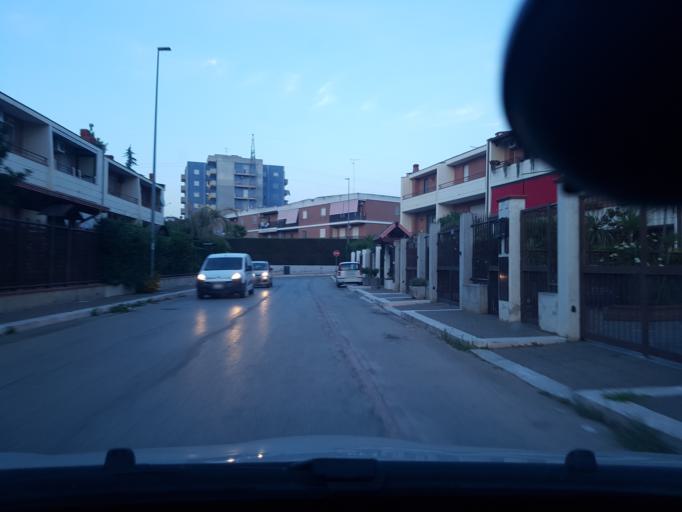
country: IT
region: Apulia
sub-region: Provincia di Foggia
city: Cerignola
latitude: 41.2606
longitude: 15.8793
